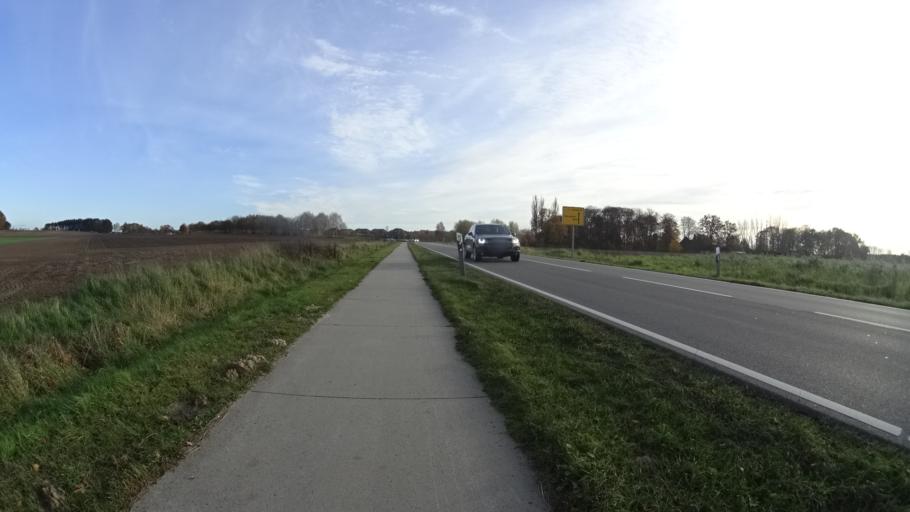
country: DE
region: Lower Saxony
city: Wendisch Evern
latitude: 53.2222
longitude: 10.4610
